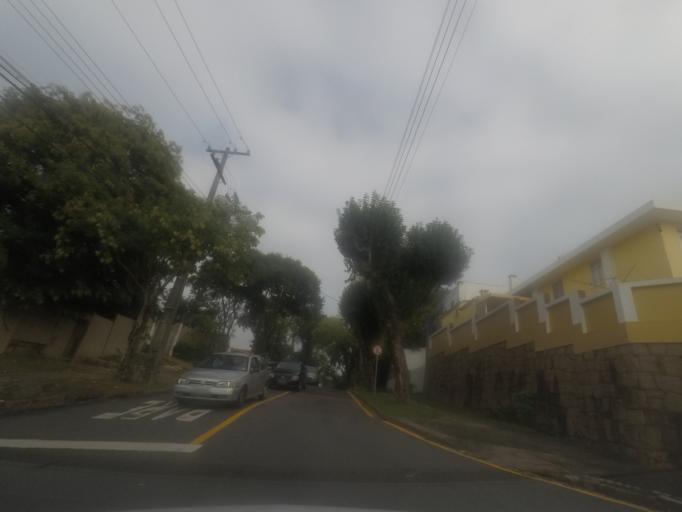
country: BR
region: Parana
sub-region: Curitiba
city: Curitiba
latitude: -25.4179
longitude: -49.2878
